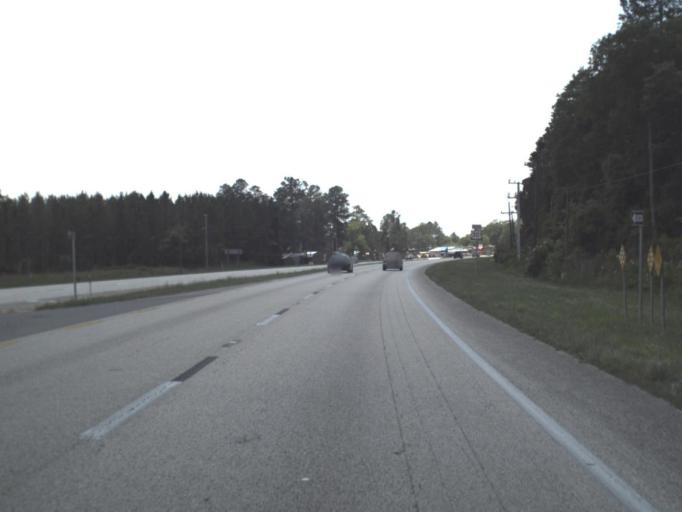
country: US
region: Florida
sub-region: Bradford County
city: Starke
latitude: 29.8914
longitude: -82.1399
